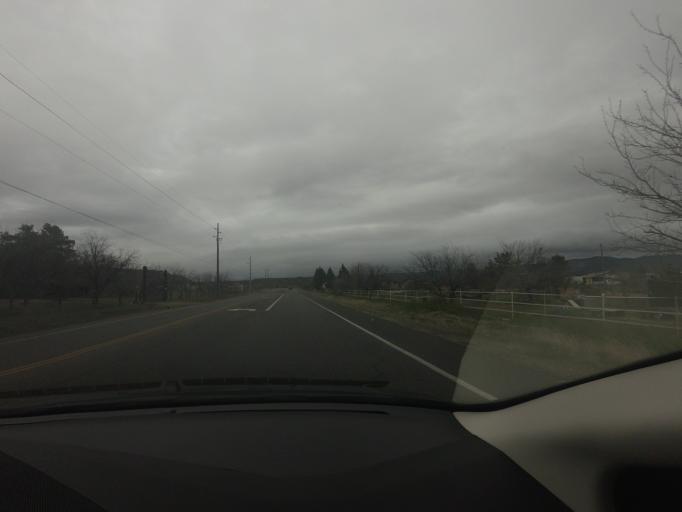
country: US
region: Arizona
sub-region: Yavapai County
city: Lake Montezuma
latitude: 34.6521
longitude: -111.7823
